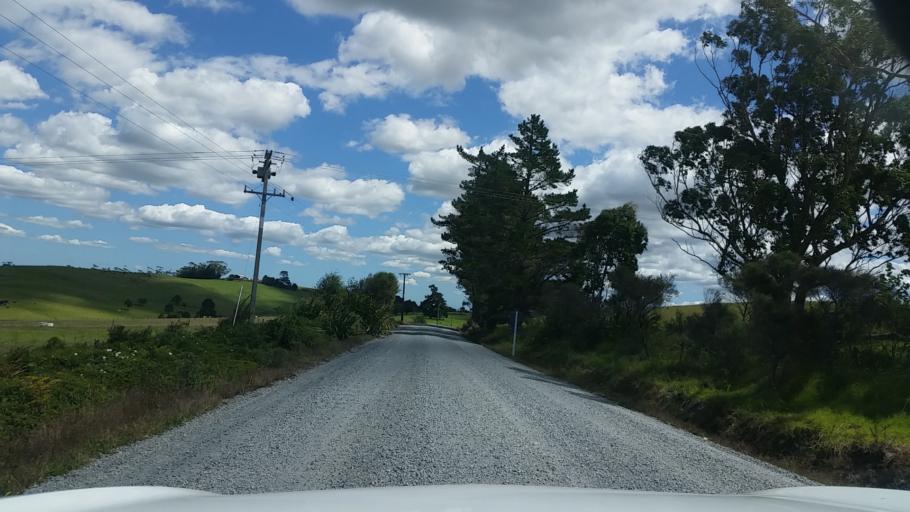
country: NZ
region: Northland
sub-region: Whangarei
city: Maungatapere
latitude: -35.6631
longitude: 174.1848
